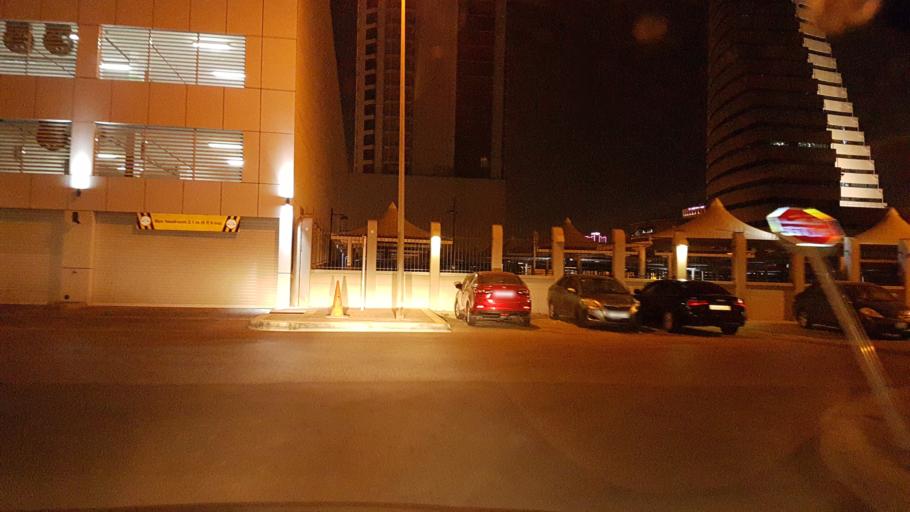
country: BH
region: Manama
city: Jidd Hafs
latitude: 26.2297
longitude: 50.5464
